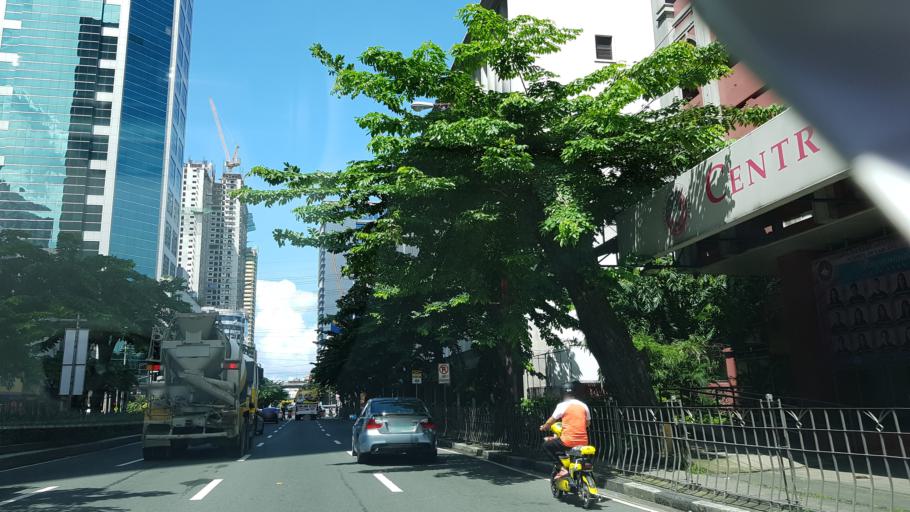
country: PH
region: Metro Manila
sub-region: Makati City
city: Makati City
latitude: 14.5606
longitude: 121.0128
